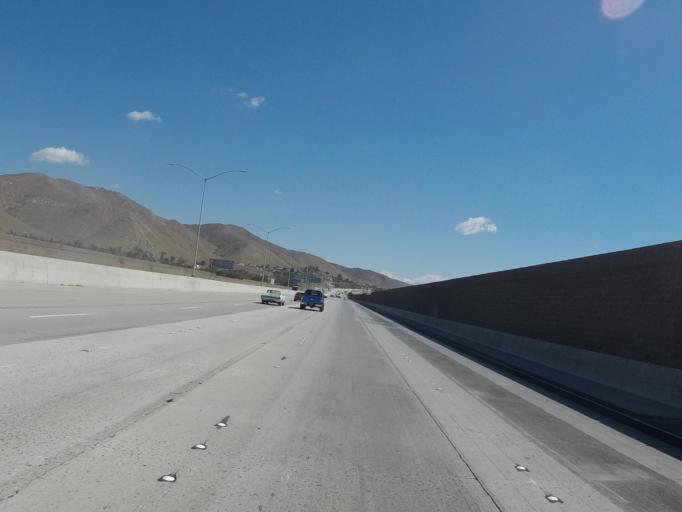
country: US
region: California
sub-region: Riverside County
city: Glen Avon
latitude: 34.0191
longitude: -117.4962
